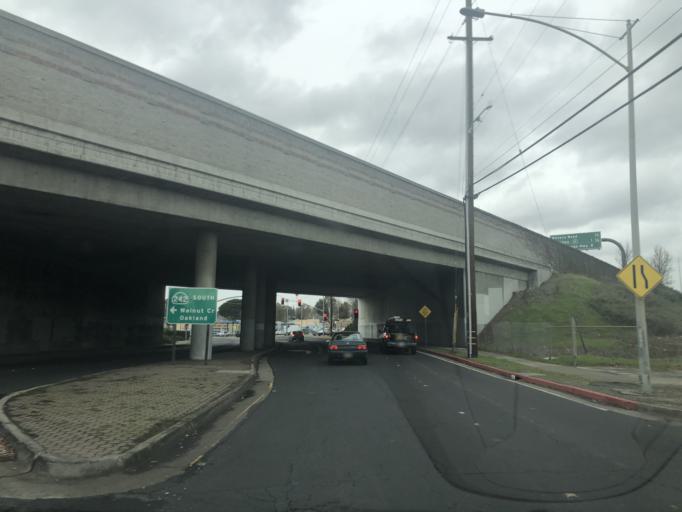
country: US
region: California
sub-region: Contra Costa County
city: Concord
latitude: 37.9882
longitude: -122.0400
